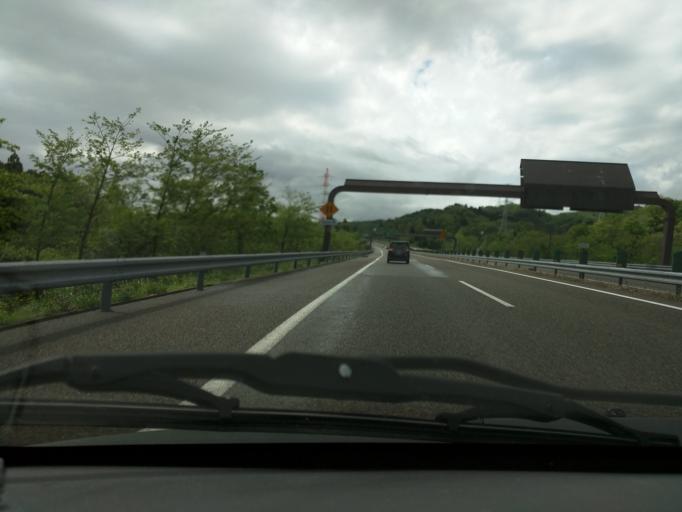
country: JP
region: Niigata
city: Joetsu
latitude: 37.1329
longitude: 138.2131
